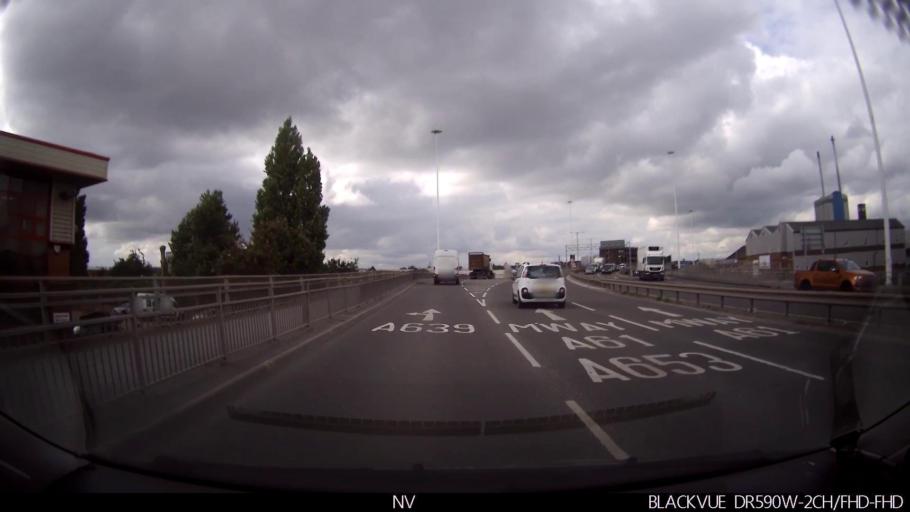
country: GB
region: England
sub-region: City and Borough of Leeds
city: Leeds
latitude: 53.7870
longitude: -1.5243
